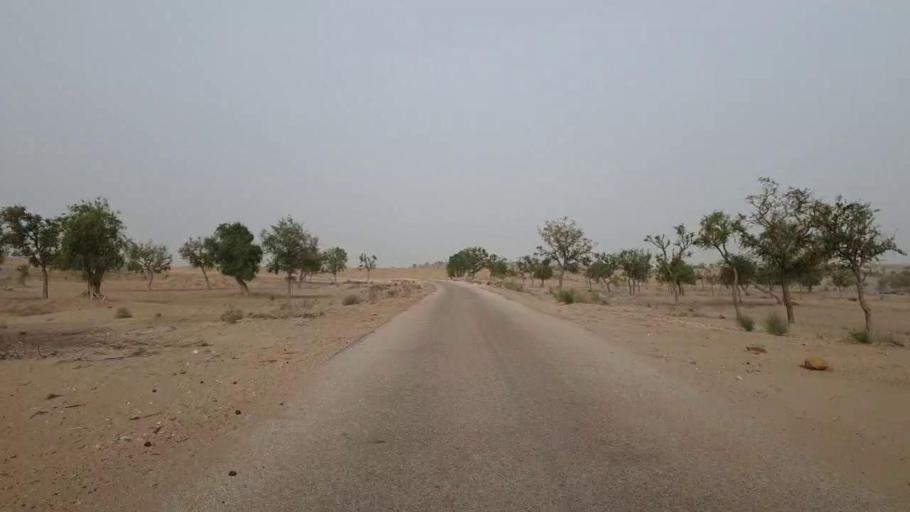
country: PK
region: Sindh
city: Islamkot
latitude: 24.5440
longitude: 70.3785
